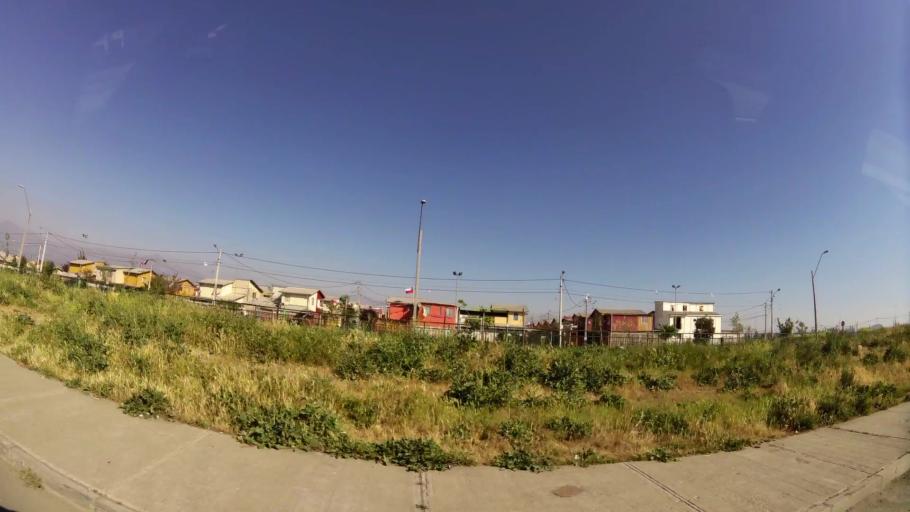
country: CL
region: Santiago Metropolitan
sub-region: Provincia de Santiago
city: La Pintana
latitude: -33.5700
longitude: -70.6106
